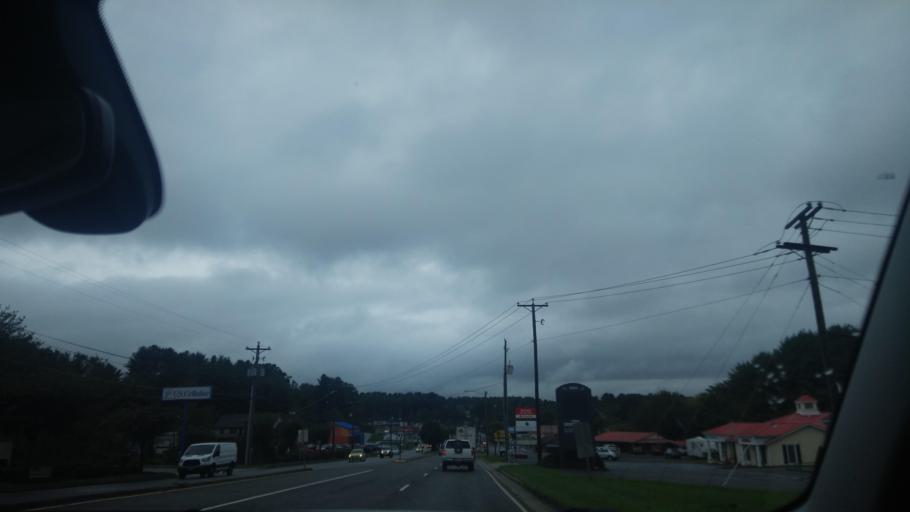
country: US
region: Virginia
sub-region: City of Galax
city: Galax
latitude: 36.6837
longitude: -80.8911
